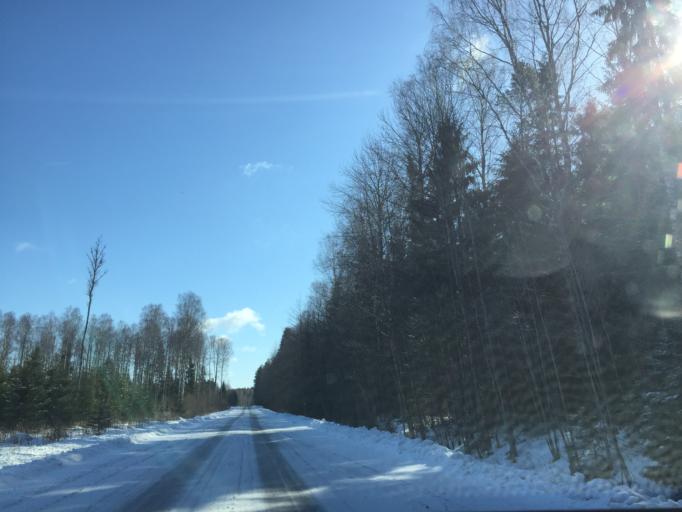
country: LV
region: Salacgrivas
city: Ainazi
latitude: 57.9976
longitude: 24.5522
